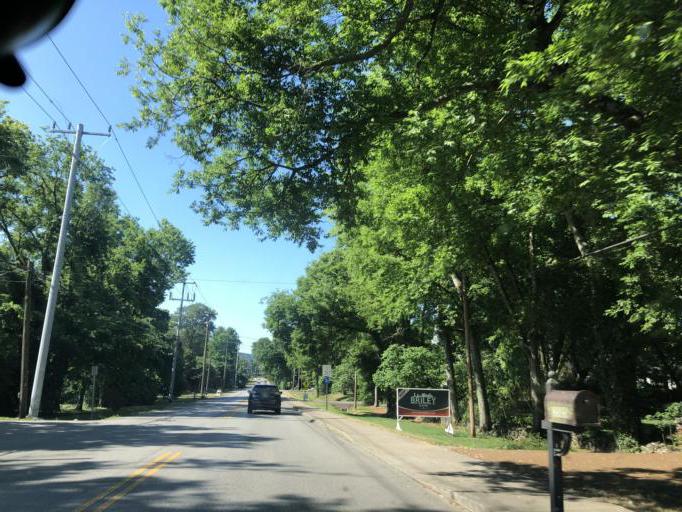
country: US
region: Tennessee
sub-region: Davidson County
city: Oak Hill
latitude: 36.1121
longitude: -86.8002
